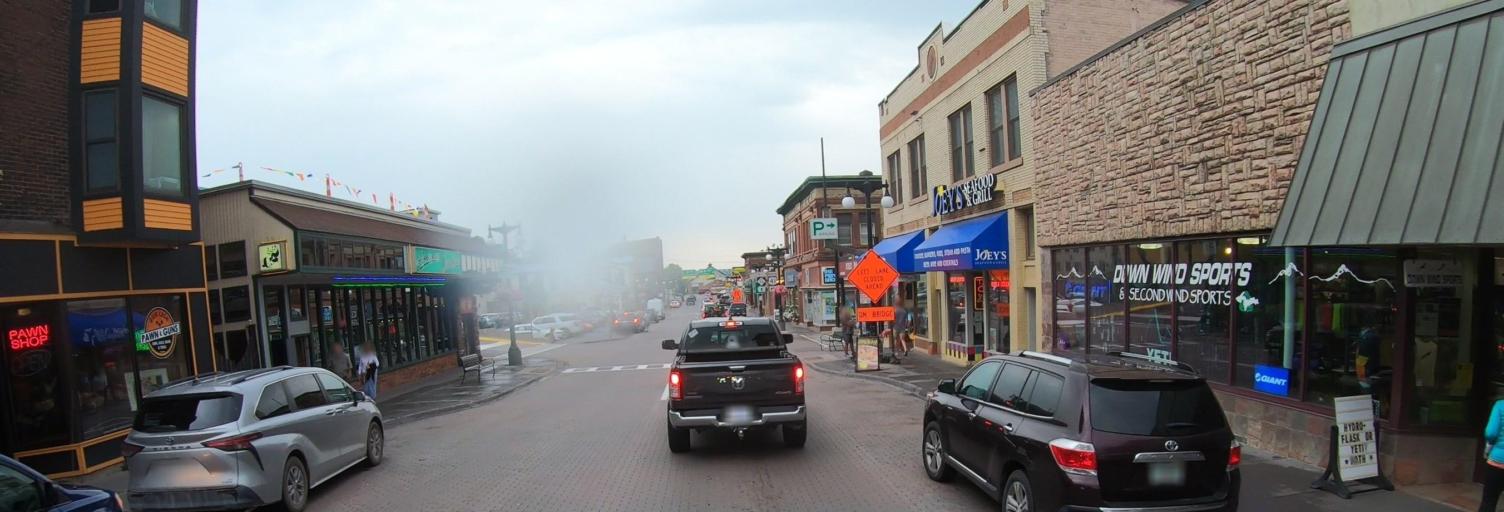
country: US
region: Michigan
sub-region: Houghton County
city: Houghton
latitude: 47.1219
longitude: -88.5700
